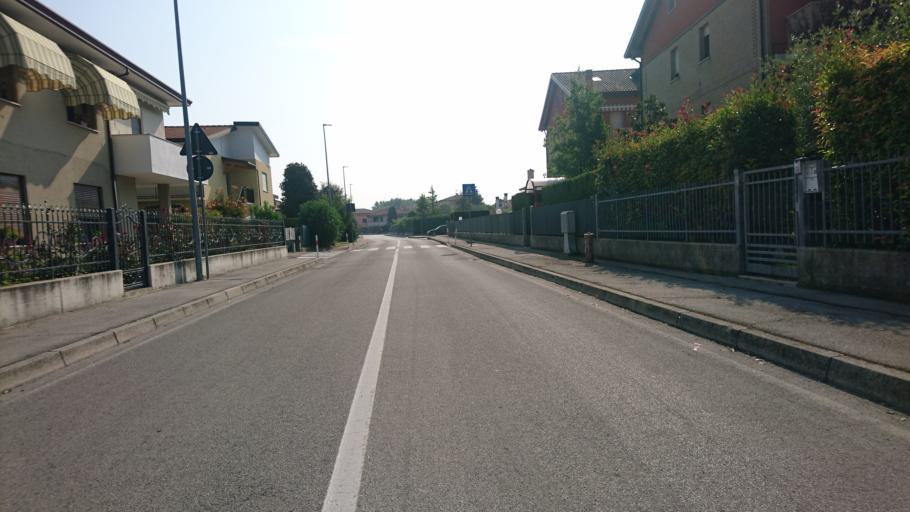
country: IT
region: Veneto
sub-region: Provincia di Padova
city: Albignasego
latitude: 45.3453
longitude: 11.8644
